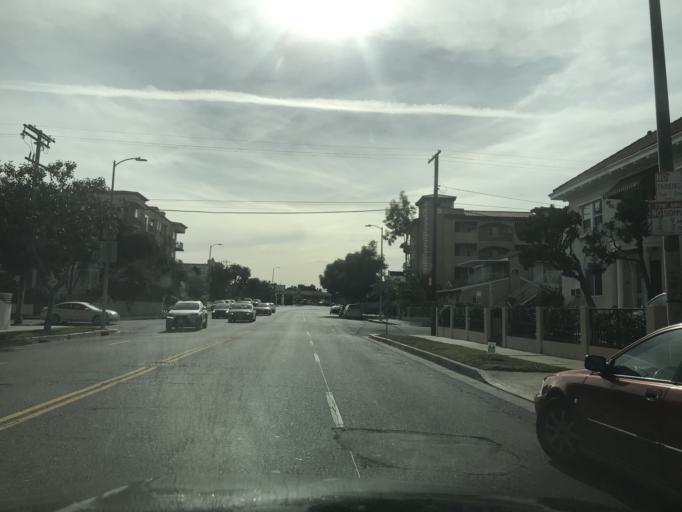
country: US
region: California
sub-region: Los Angeles County
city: Hollywood
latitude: 34.0549
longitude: -118.3143
